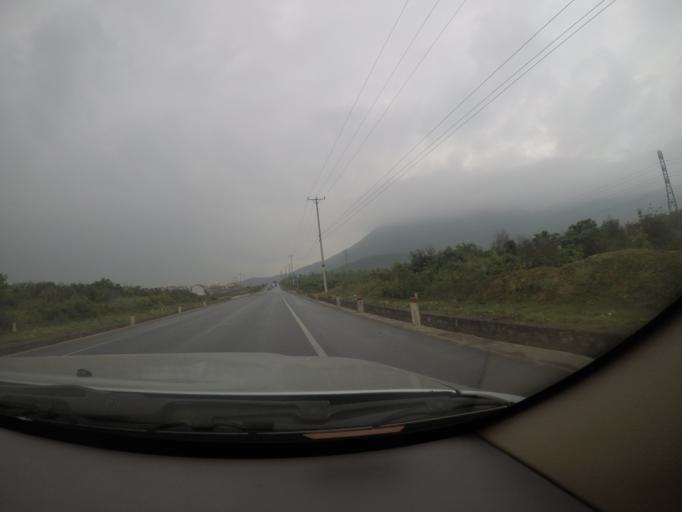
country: VN
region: Ha Tinh
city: Ky Anh
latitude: 17.9995
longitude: 106.4494
